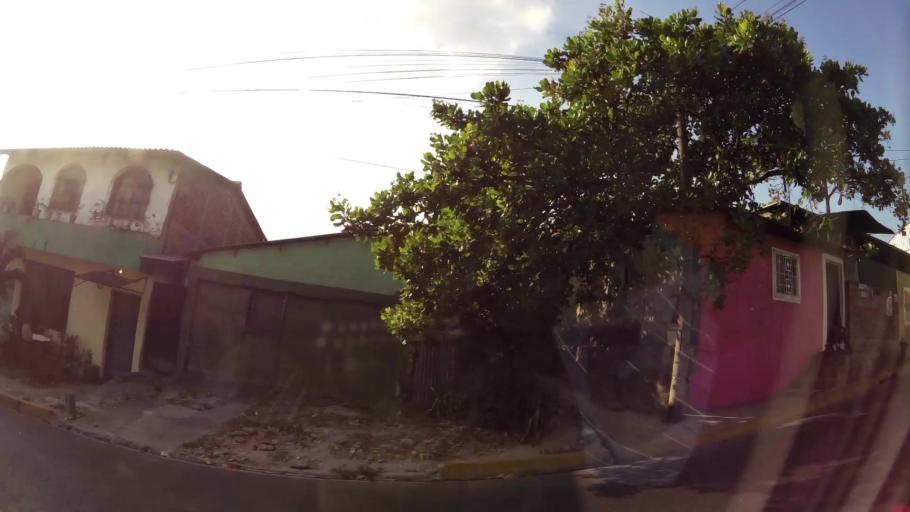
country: SV
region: San Salvador
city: San Salvador
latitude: 13.6977
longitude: -89.1768
